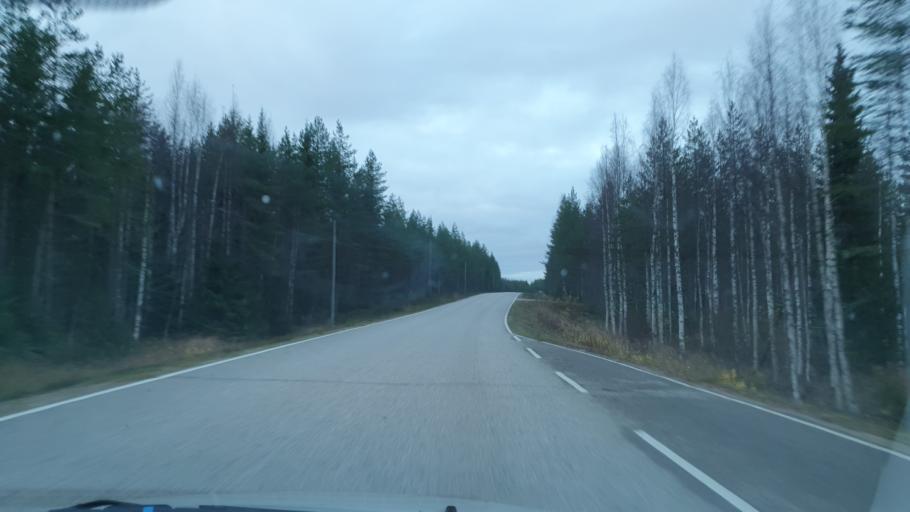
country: FI
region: Kainuu
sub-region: Kajaani
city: Ristijaervi
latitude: 64.4322
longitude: 28.3688
